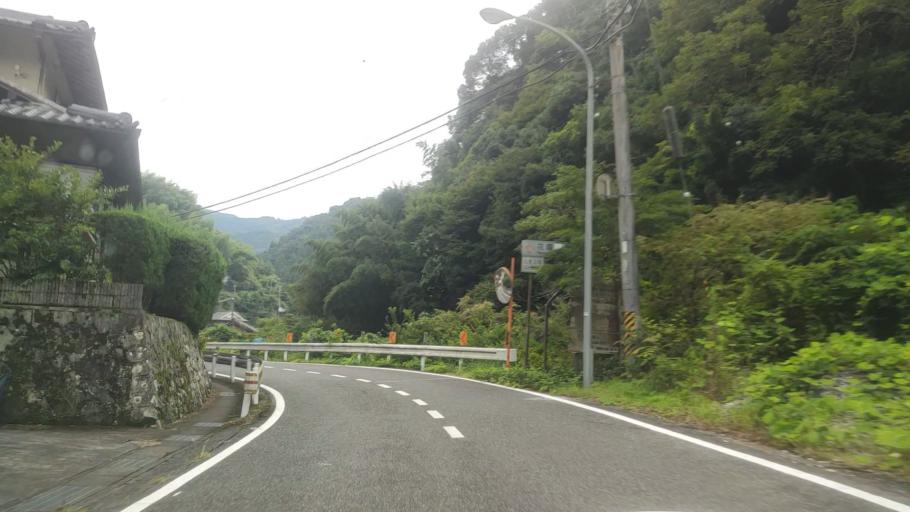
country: JP
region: Wakayama
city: Hashimoto
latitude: 34.2644
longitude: 135.5507
